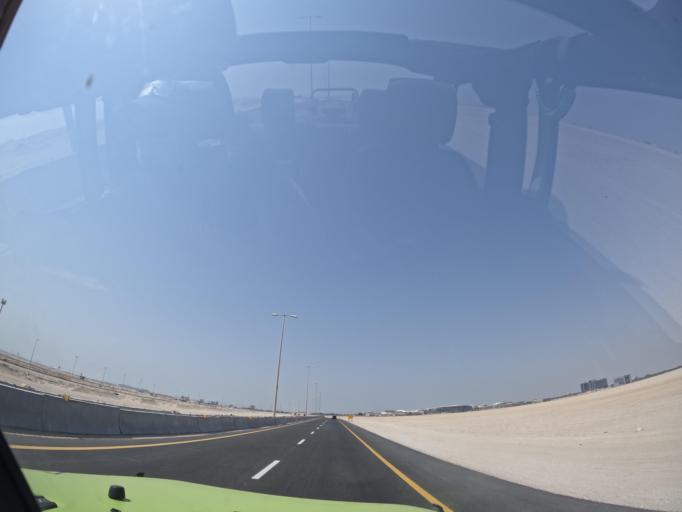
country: AE
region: Abu Dhabi
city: Abu Dhabi
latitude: 24.3821
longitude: 54.5844
